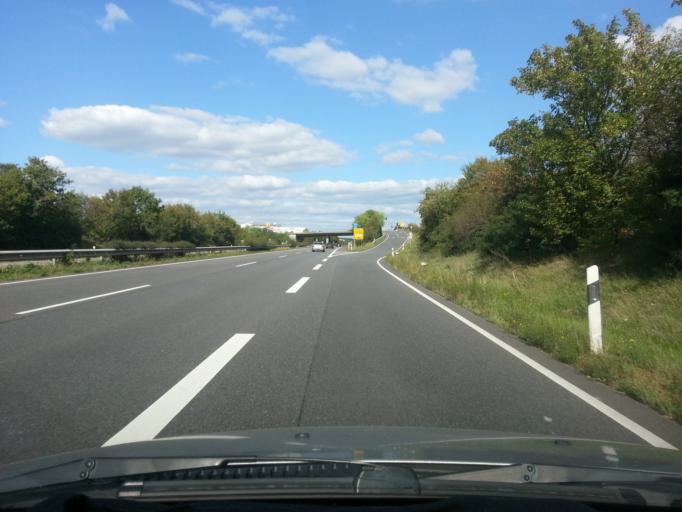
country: DE
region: Baden-Wuerttemberg
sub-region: Karlsruhe Region
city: Hockenheim
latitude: 49.3229
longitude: 8.5391
